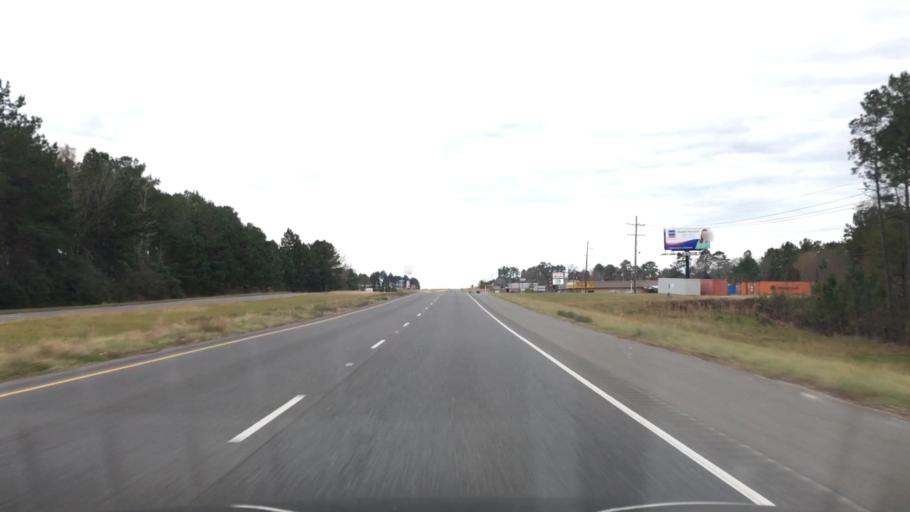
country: US
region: Louisiana
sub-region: Vernon Parish
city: New Llano
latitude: 31.0967
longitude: -93.2698
